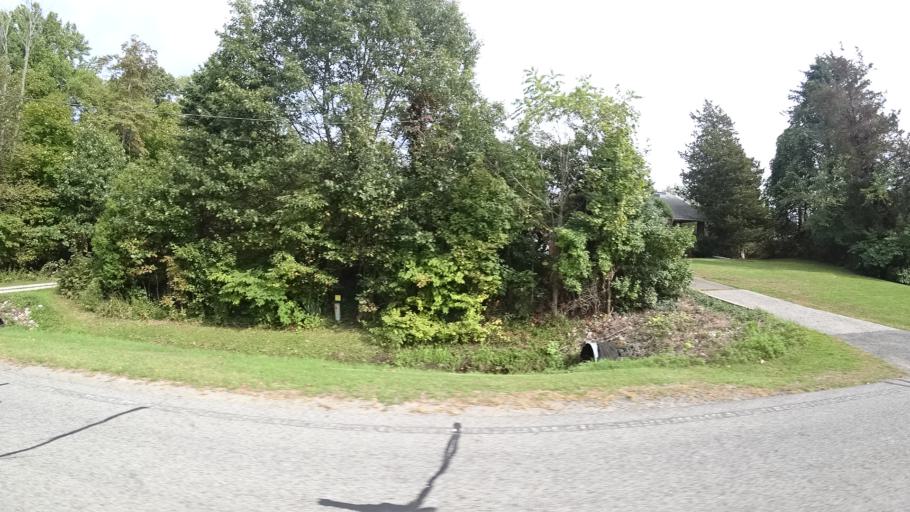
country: US
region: Indiana
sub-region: LaPorte County
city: Long Beach
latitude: 41.7275
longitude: -86.8360
